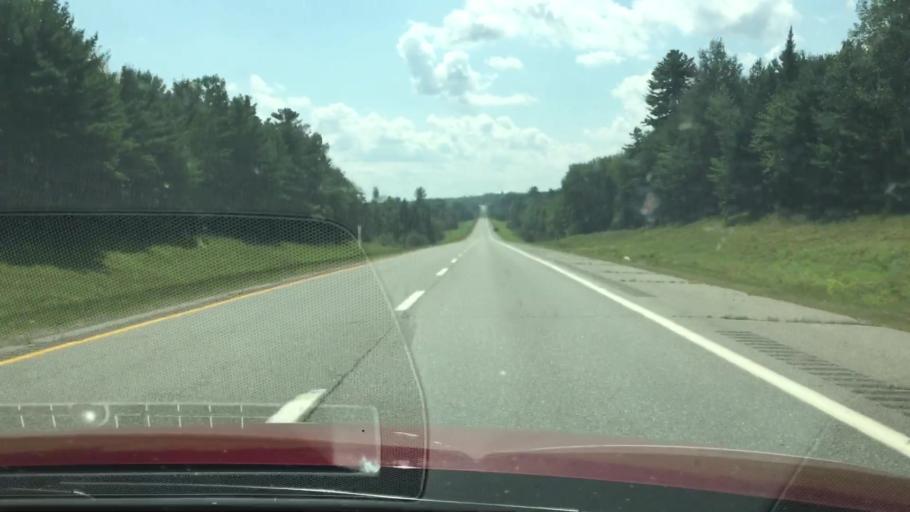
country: US
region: Maine
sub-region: Penobscot County
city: Lincoln
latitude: 45.4787
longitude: -68.5753
